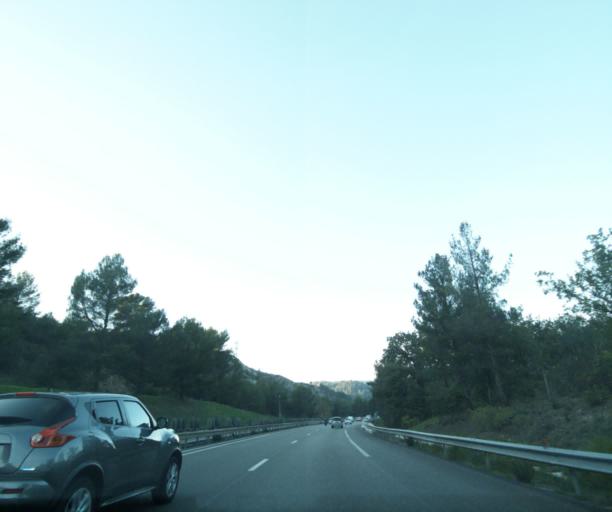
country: FR
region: Provence-Alpes-Cote d'Azur
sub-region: Departement des Bouches-du-Rhone
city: Roquevaire
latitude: 43.3597
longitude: 5.6157
